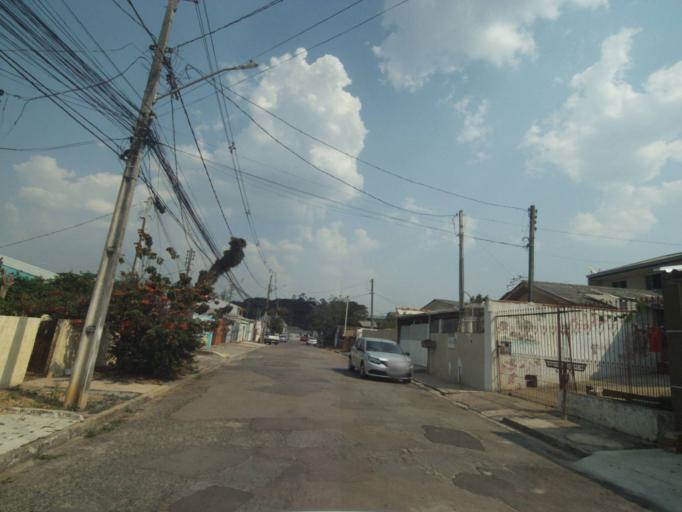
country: BR
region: Parana
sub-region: Sao Jose Dos Pinhais
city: Sao Jose dos Pinhais
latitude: -25.5424
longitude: -49.2410
